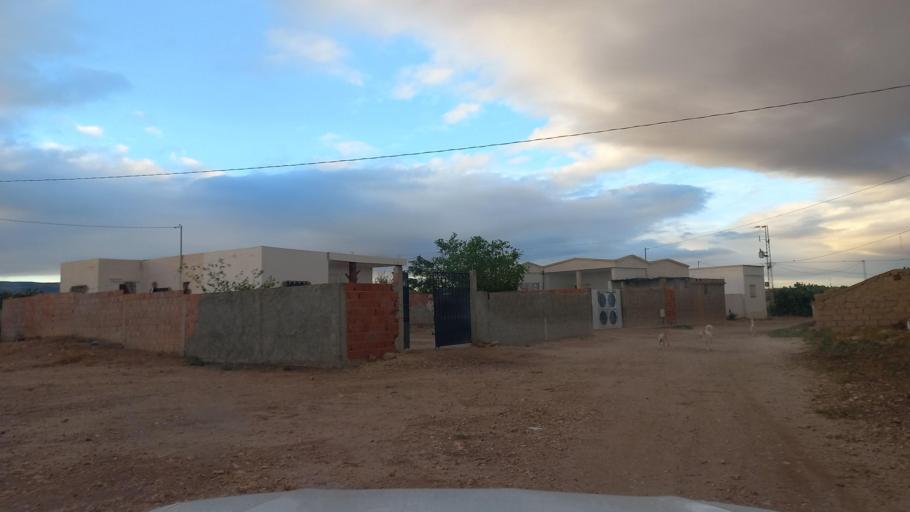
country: TN
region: Al Qasrayn
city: Kasserine
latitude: 35.2595
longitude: 8.9422
